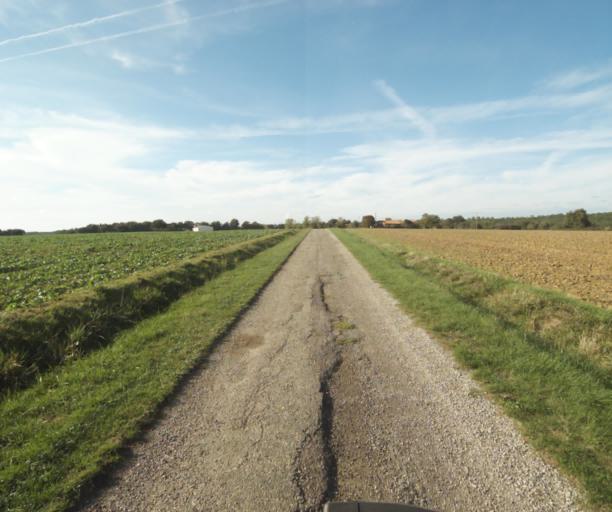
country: FR
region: Midi-Pyrenees
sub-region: Departement du Tarn-et-Garonne
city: Finhan
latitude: 43.9272
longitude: 1.1363
